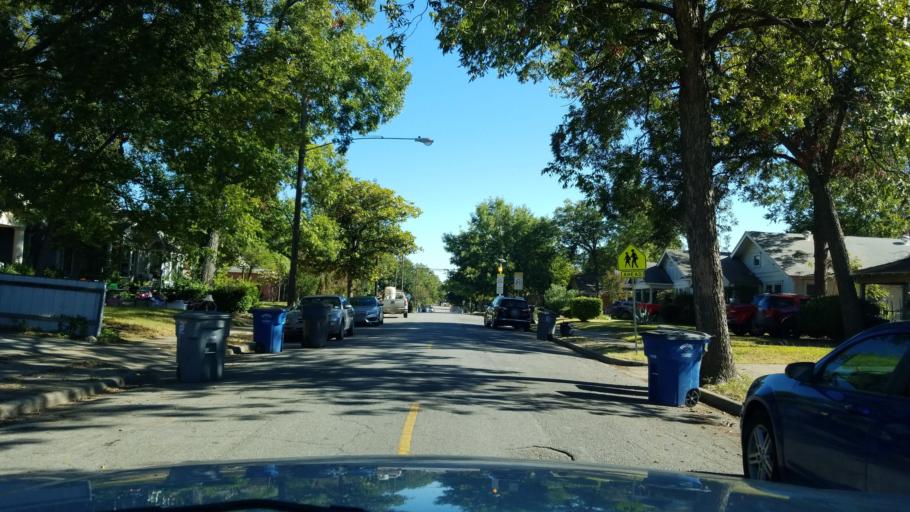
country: US
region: Texas
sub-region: Dallas County
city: Highland Park
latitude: 32.7974
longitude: -96.7484
